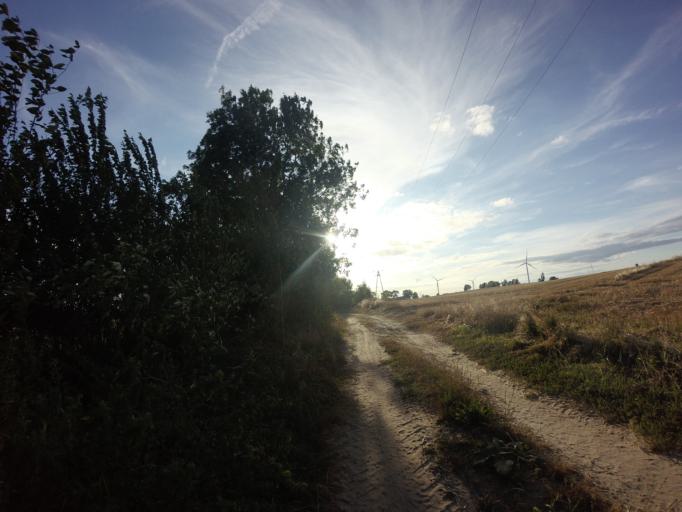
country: PL
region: West Pomeranian Voivodeship
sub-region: Powiat choszczenski
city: Krzecin
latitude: 53.1090
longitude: 15.4563
